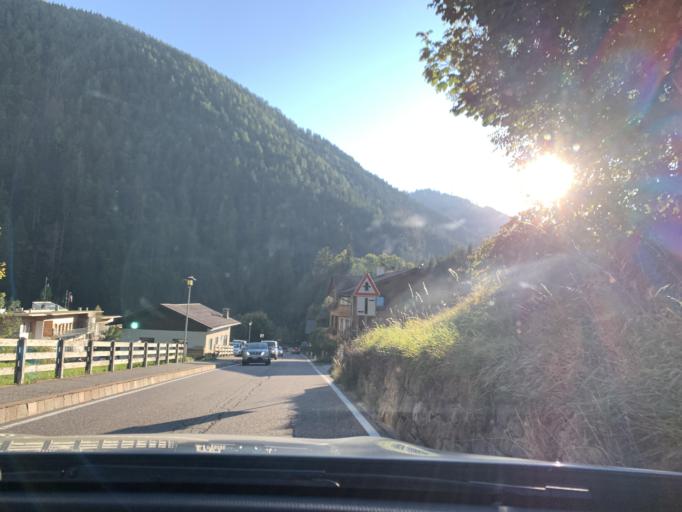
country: IT
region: Trentino-Alto Adige
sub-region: Bolzano
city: Nova Levante
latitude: 46.4290
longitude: 11.5402
